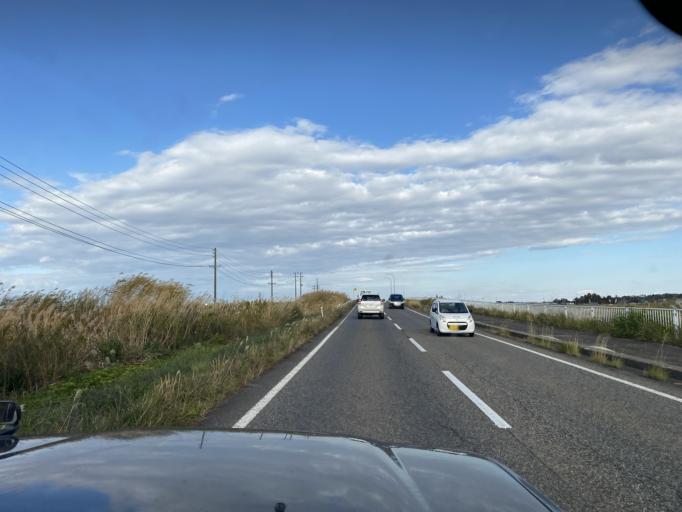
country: JP
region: Niigata
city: Niitsu-honcho
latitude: 37.7755
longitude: 139.1061
